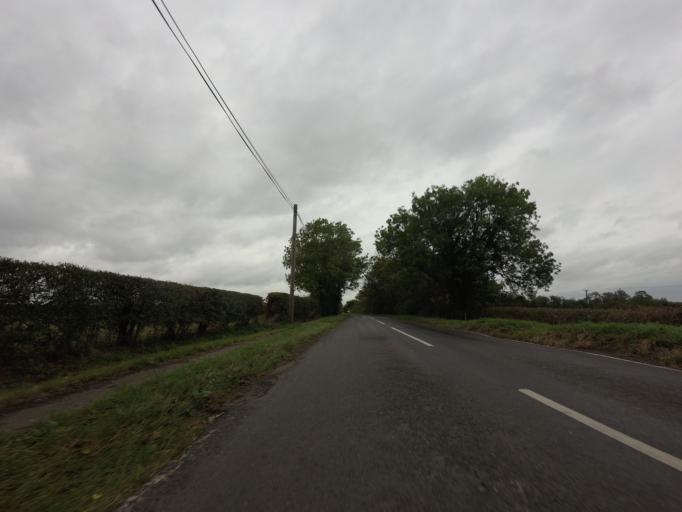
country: GB
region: England
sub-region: Cambridgeshire
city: Comberton
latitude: 52.1527
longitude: 0.0148
